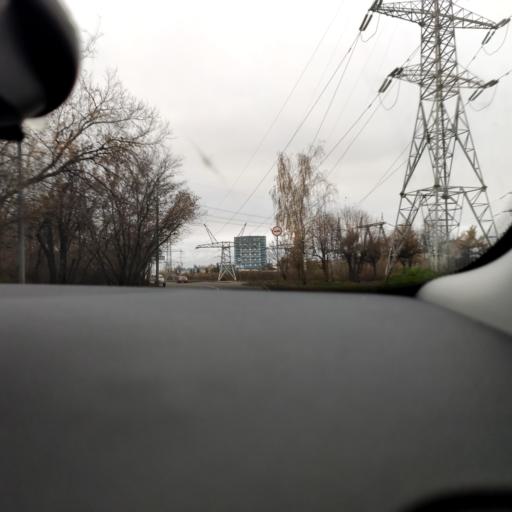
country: RU
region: Moscow
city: Kapotnya
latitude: 55.6678
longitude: 37.8075
